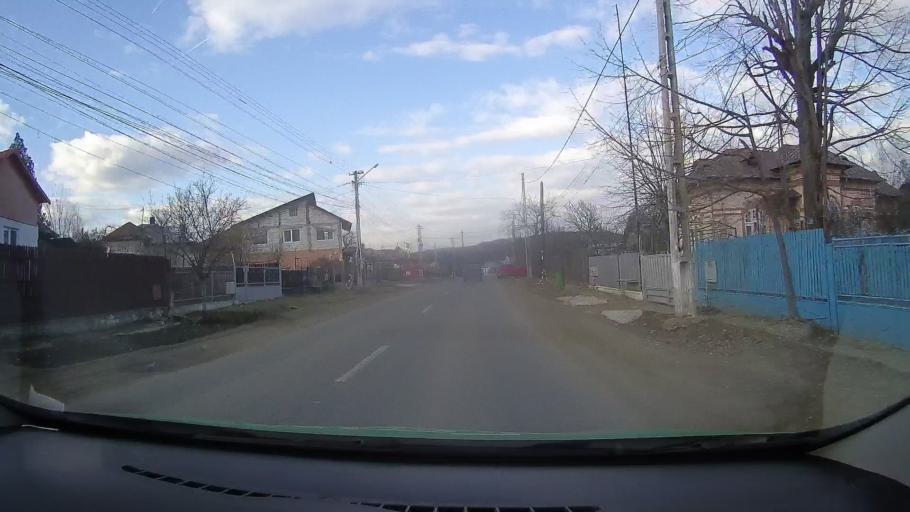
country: RO
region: Dambovita
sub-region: Comuna Gura Ocnitei
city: Gura Ocnitei
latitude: 44.9354
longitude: 25.5620
